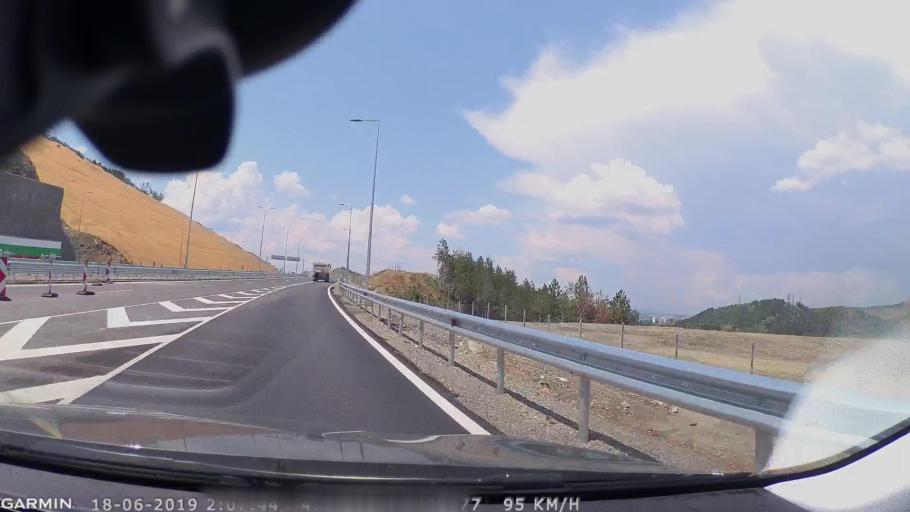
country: BG
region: Blagoevgrad
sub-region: Obshtina Blagoevgrad
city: Blagoevgrad
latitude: 41.9661
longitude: 23.0937
